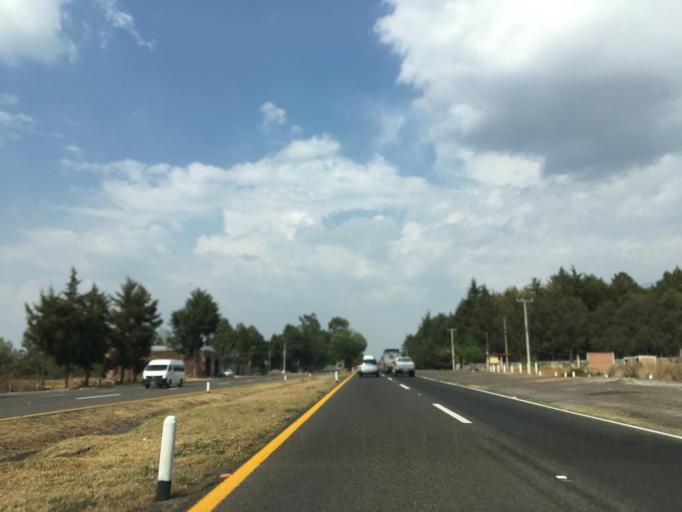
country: MX
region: Michoacan
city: Patzcuaro
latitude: 19.5331
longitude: -101.5520
